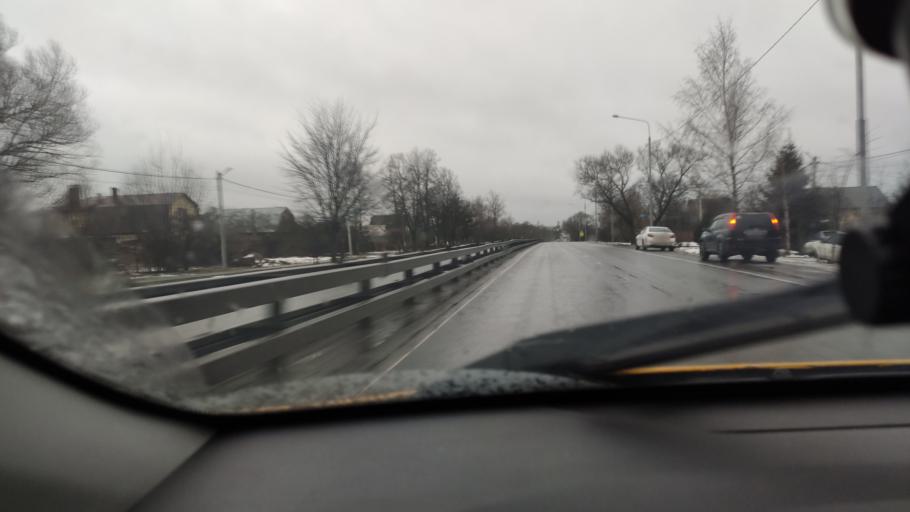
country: RU
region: Moskovskaya
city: Troitsk
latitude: 55.3062
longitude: 37.2220
